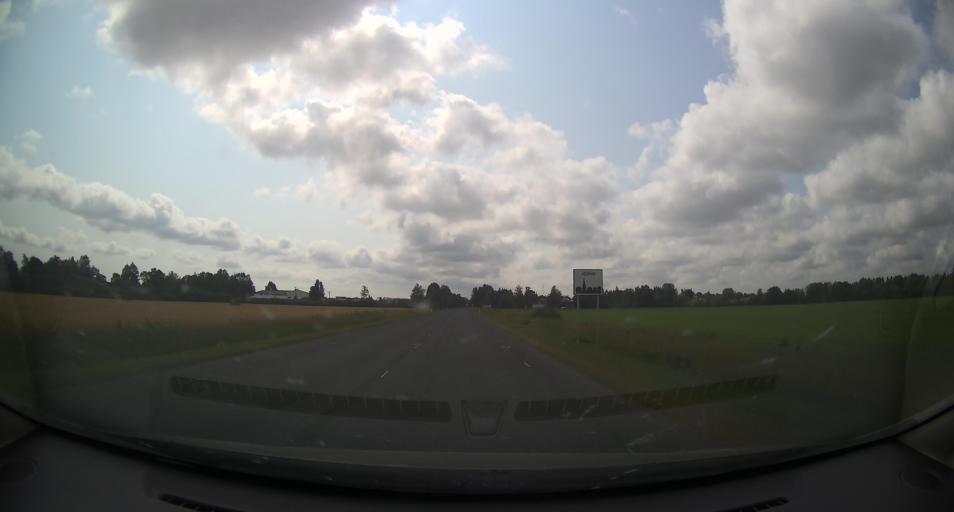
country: EE
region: Paernumaa
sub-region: Audru vald
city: Audru
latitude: 58.4797
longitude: 24.3338
